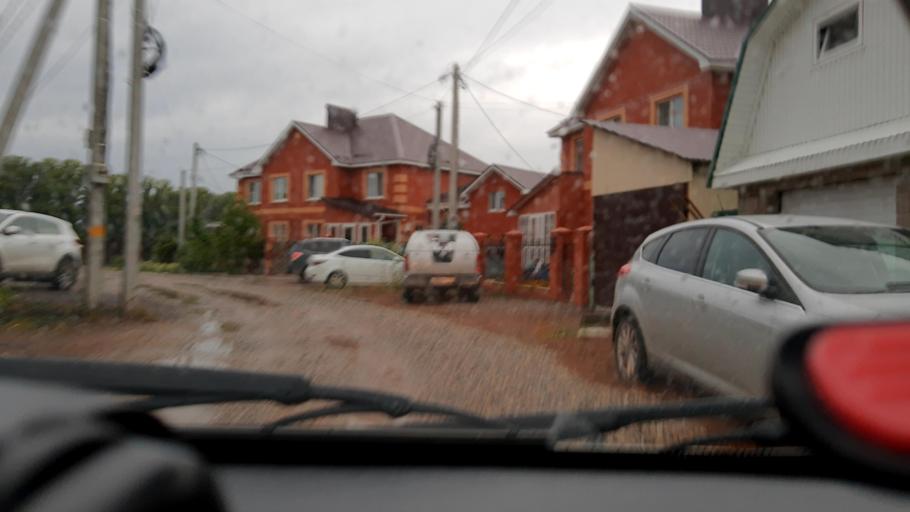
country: RU
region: Bashkortostan
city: Ufa
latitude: 54.6287
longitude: 55.9229
